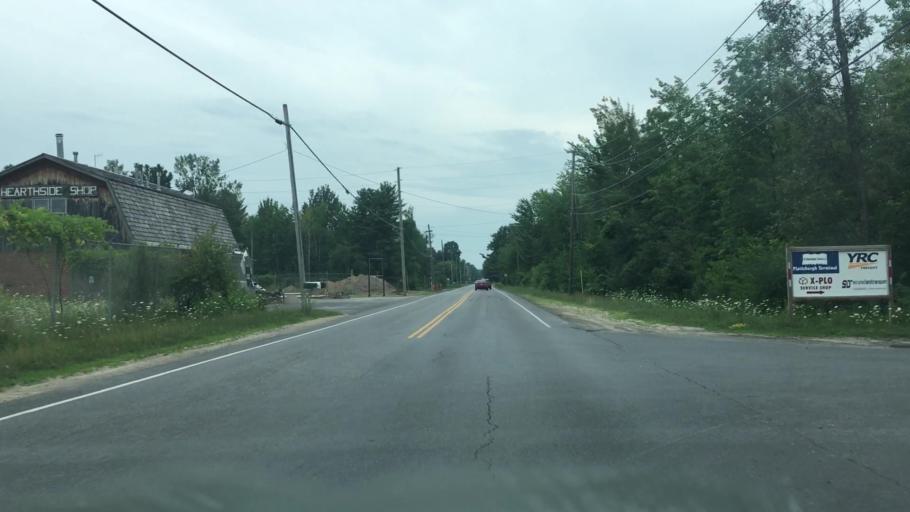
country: US
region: New York
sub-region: Clinton County
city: Plattsburgh West
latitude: 44.6624
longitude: -73.5089
